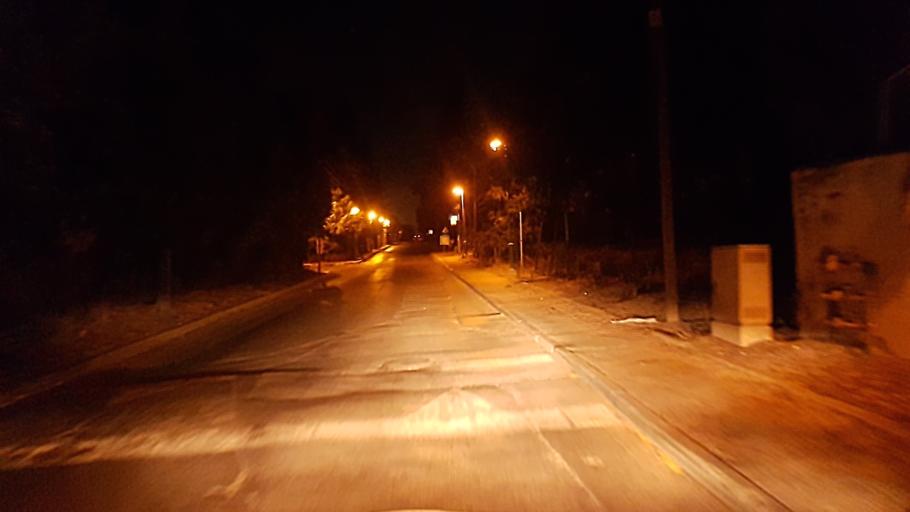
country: IL
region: Central District
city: Hod HaSharon
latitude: 32.1641
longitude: 34.8760
